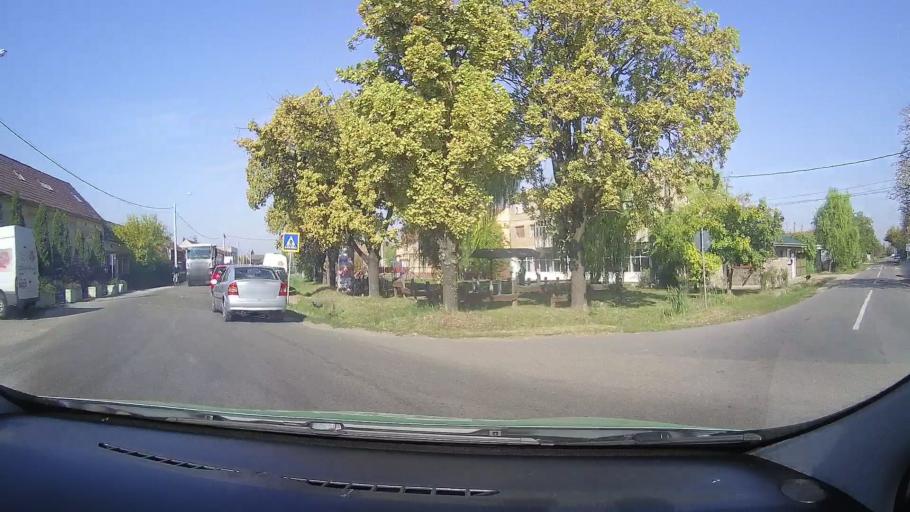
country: RO
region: Bihor
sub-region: Municipiul Salonta
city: Salonta
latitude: 46.7967
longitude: 21.6656
